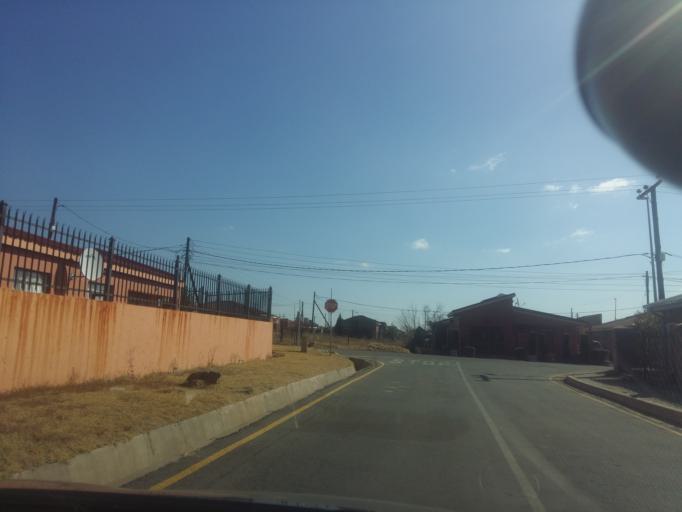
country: LS
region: Maseru
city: Maseru
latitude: -29.3459
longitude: 27.4550
